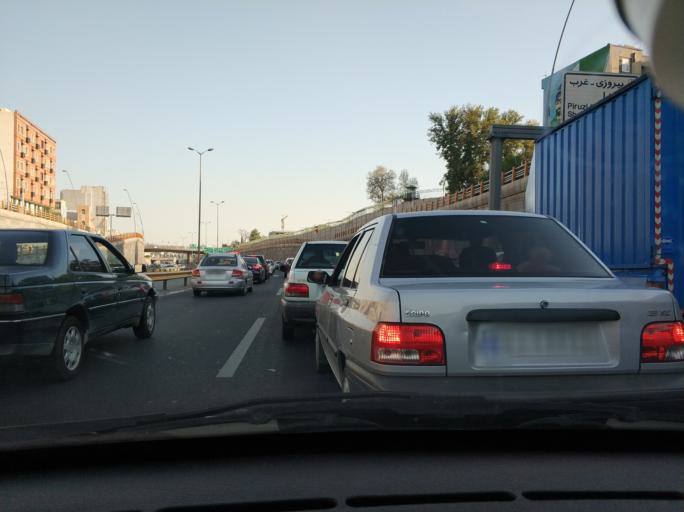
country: IR
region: Tehran
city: Tehran
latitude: 35.6960
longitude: 51.4566
